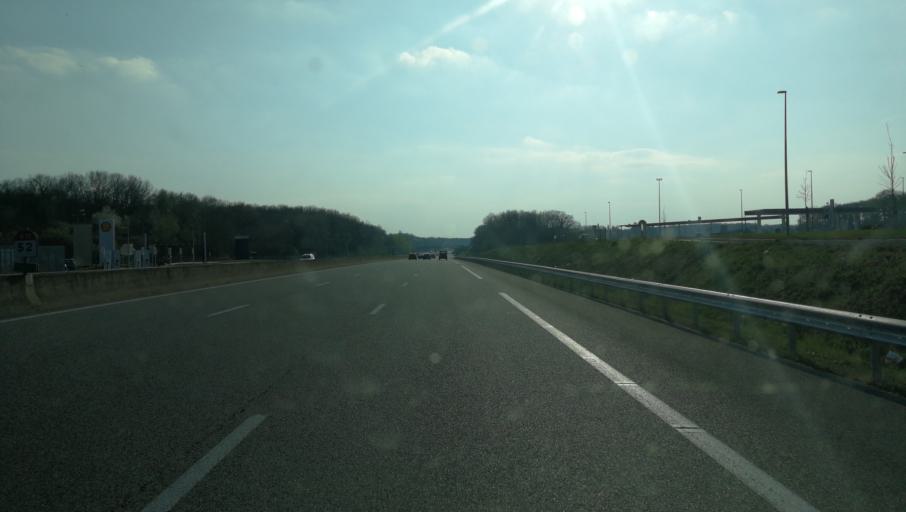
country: FR
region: Centre
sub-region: Departement d'Eure-et-Loir
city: Nogent-le-Phaye
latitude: 48.4681
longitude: 1.5791
